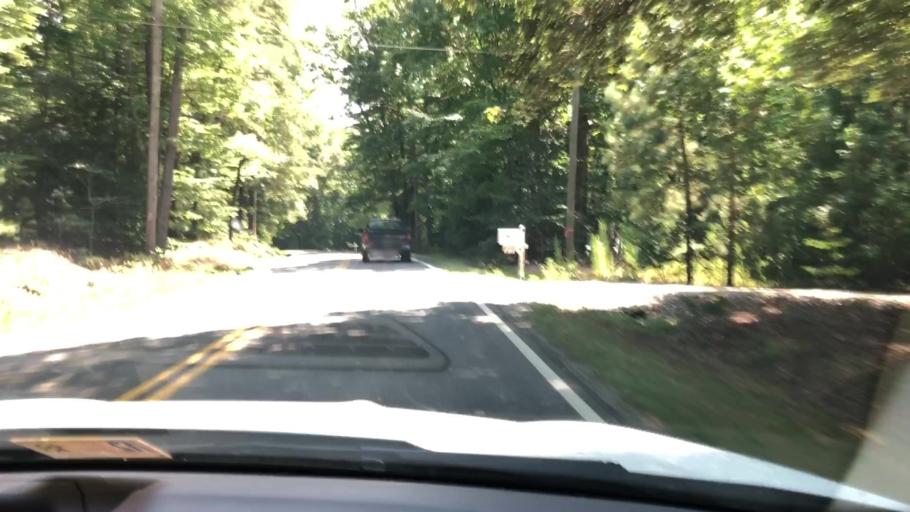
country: US
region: Virginia
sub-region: King William County
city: West Point
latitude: 37.5055
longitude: -76.8223
